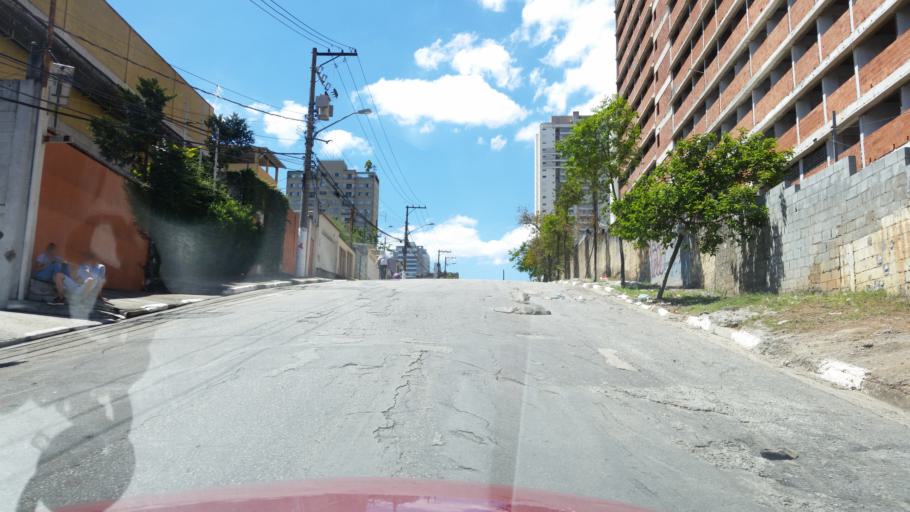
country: BR
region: Sao Paulo
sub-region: Diadema
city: Diadema
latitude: -23.6312
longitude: -46.6702
